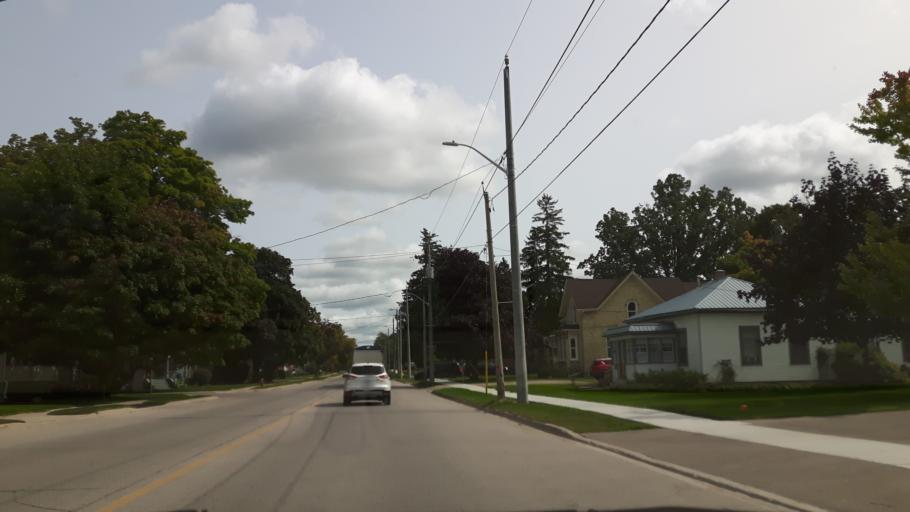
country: CA
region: Ontario
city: Bluewater
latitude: 43.6157
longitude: -81.5366
